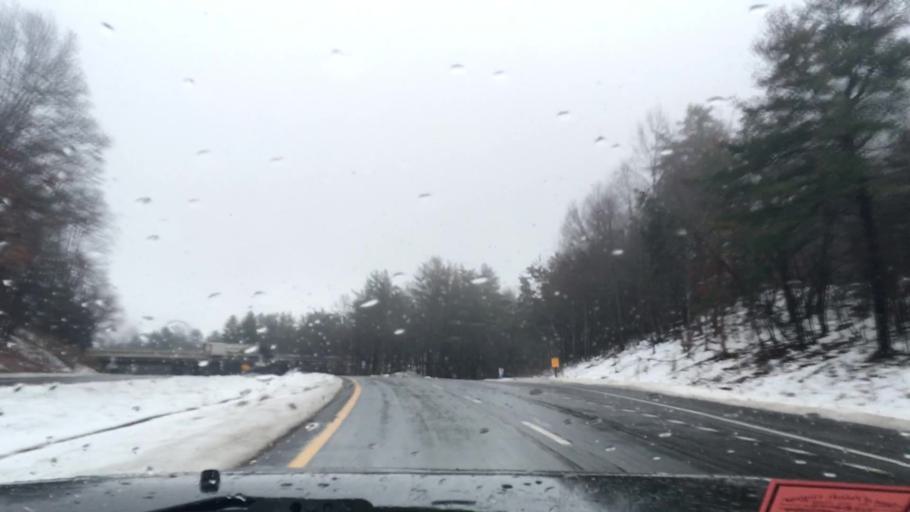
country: US
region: Virginia
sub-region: Pulaski County
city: Pulaski
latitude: 37.0278
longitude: -80.7313
